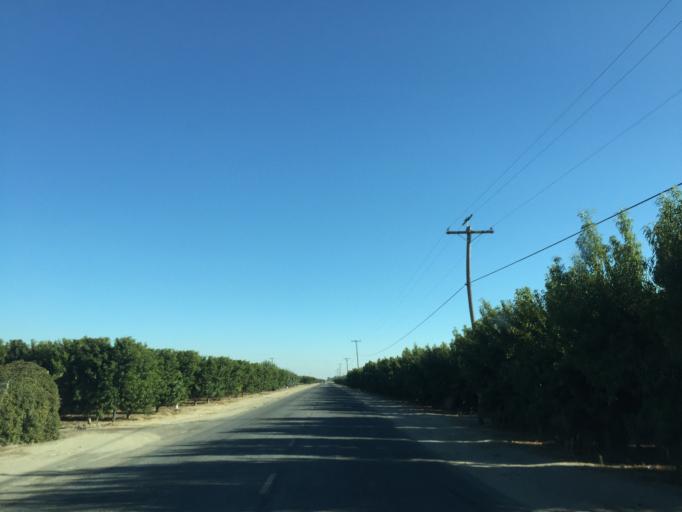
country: US
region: California
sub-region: Tulare County
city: London
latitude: 36.4720
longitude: -119.4386
